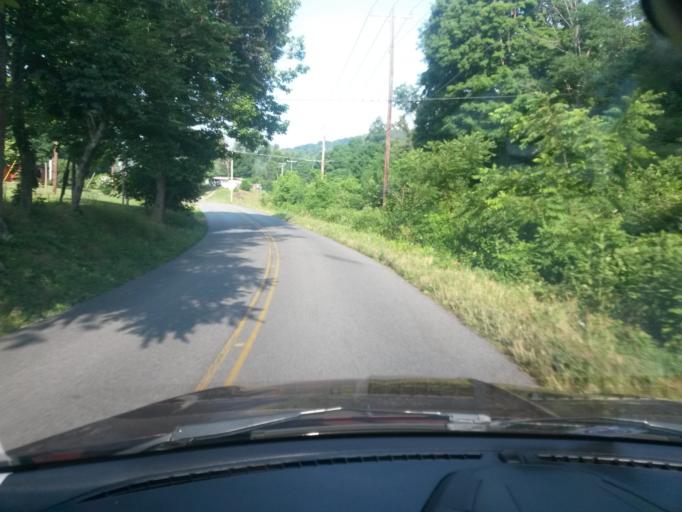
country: US
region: Virginia
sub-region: Giles County
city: Narrows
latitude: 37.3685
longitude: -80.8118
